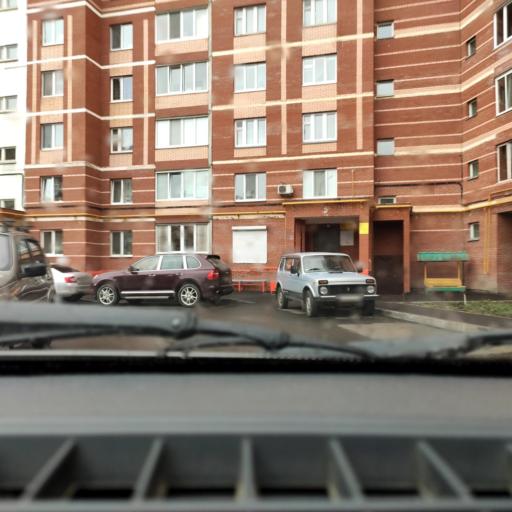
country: RU
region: Bashkortostan
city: Ufa
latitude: 54.7785
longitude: 56.0746
